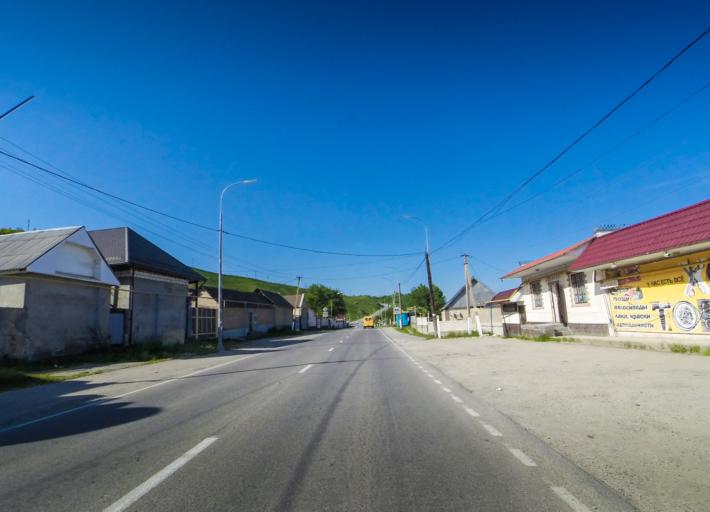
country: RU
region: Kabardino-Balkariya
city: Aushiger
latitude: 43.3996
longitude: 43.7422
